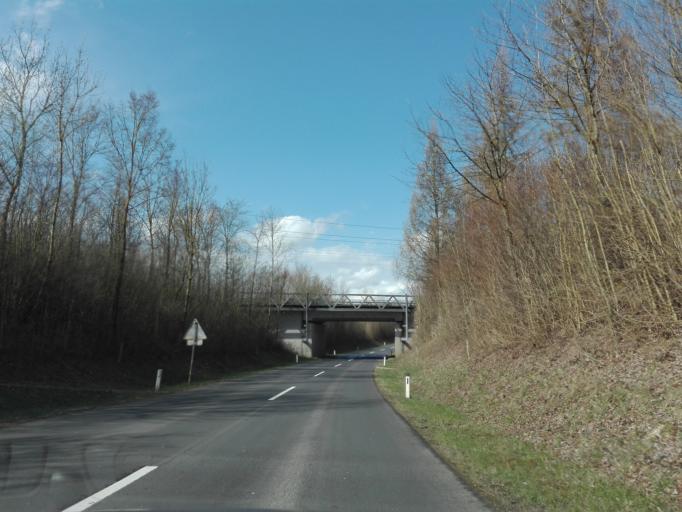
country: AT
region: Upper Austria
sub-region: Wels-Land
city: Holzhausen
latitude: 48.2153
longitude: 14.1288
